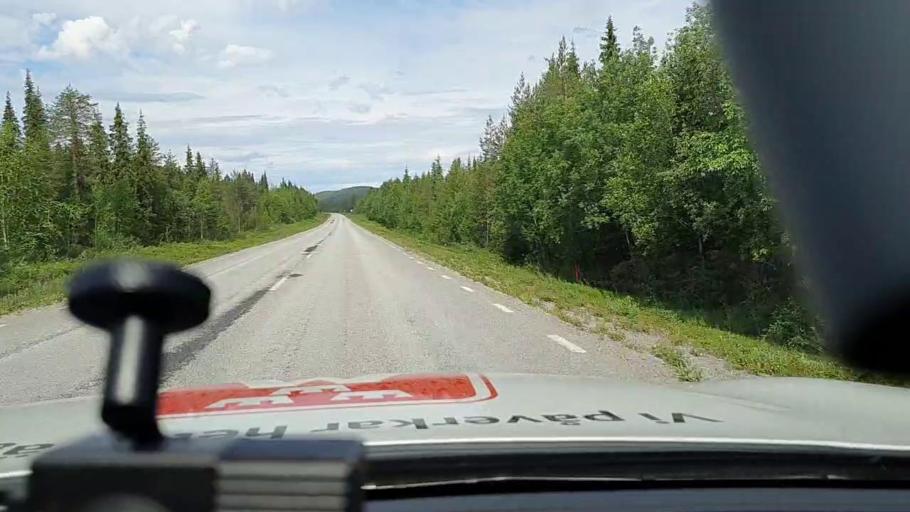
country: SE
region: Norrbotten
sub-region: Jokkmokks Kommun
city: Jokkmokk
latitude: 66.5487
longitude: 20.1264
